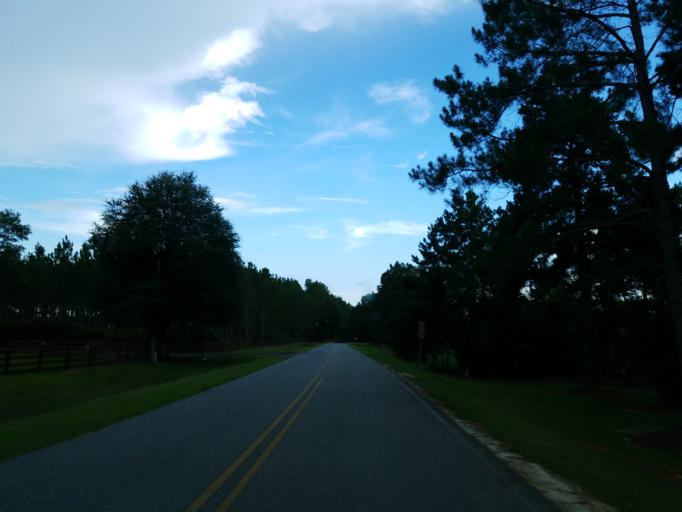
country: US
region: Georgia
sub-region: Tift County
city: Omega
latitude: 31.2585
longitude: -83.5138
